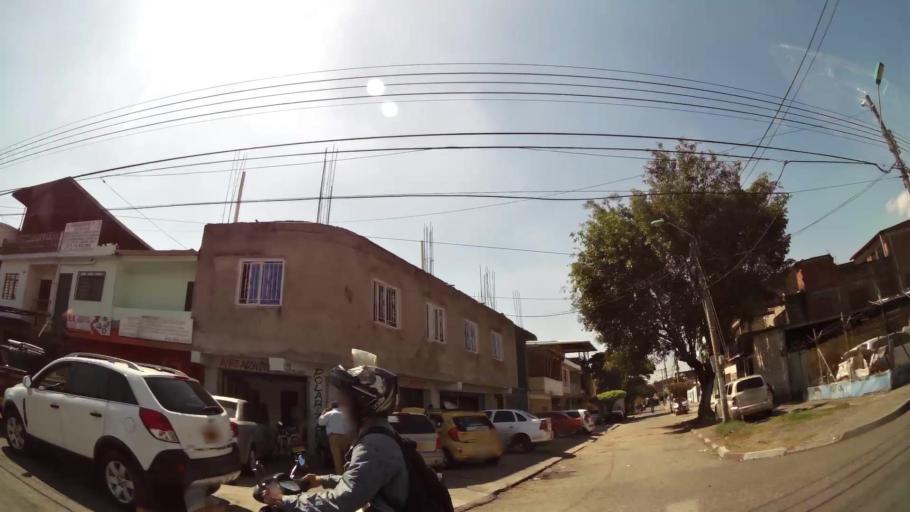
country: CO
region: Valle del Cauca
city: Cali
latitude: 3.4416
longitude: -76.4968
